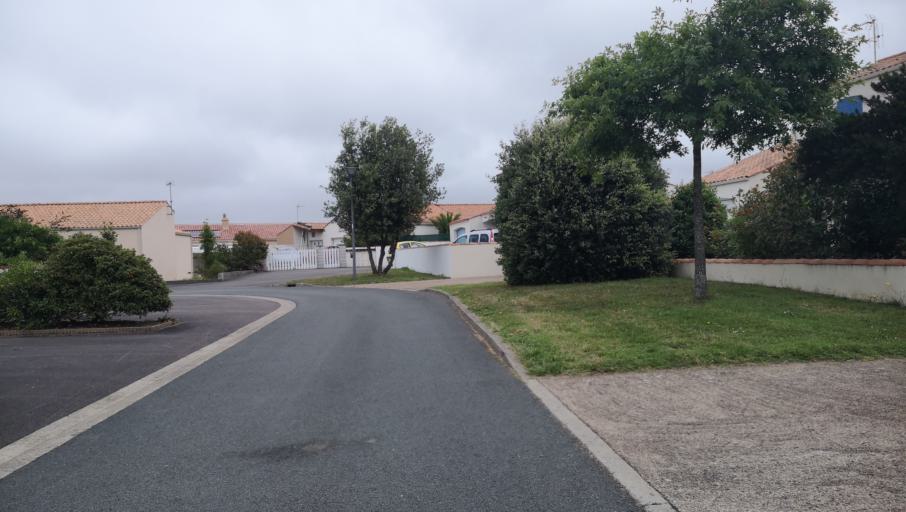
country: FR
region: Pays de la Loire
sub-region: Departement de la Vendee
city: Les Sables-d'Olonne
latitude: 46.5104
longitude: -1.7806
